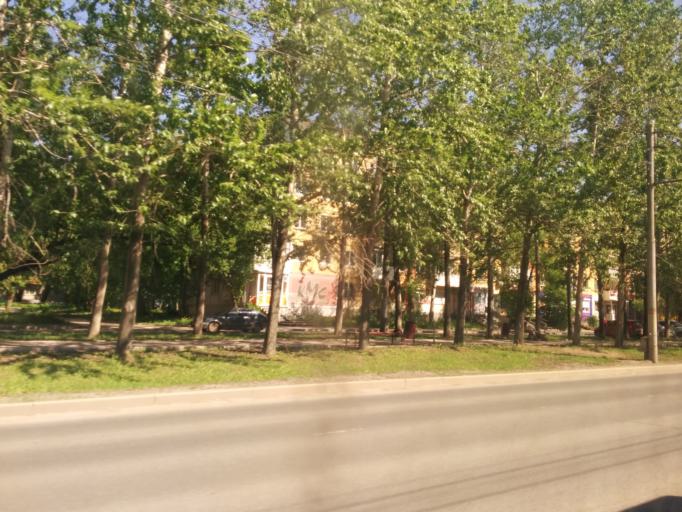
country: RU
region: Perm
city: Perm
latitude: 58.0025
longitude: 56.2867
